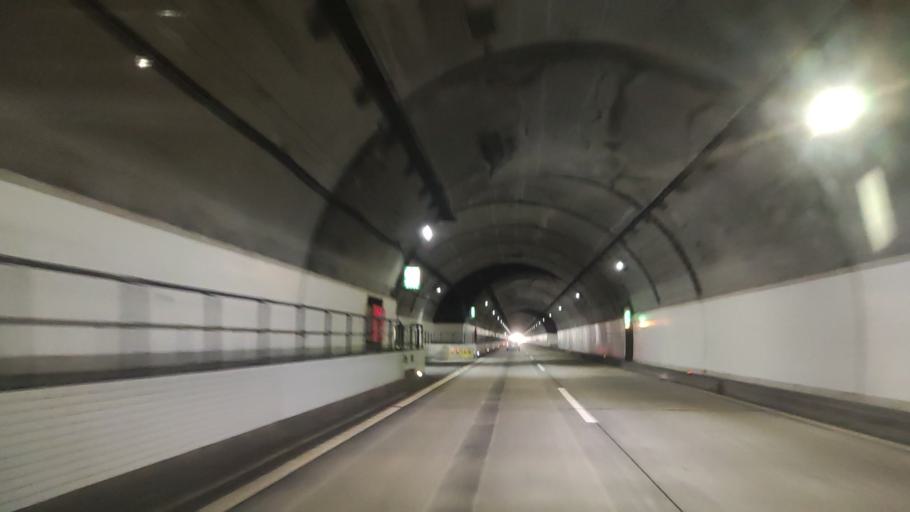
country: JP
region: Ehime
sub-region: Shikoku-chuo Shi
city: Matsuyama
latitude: 33.8229
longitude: 132.9692
